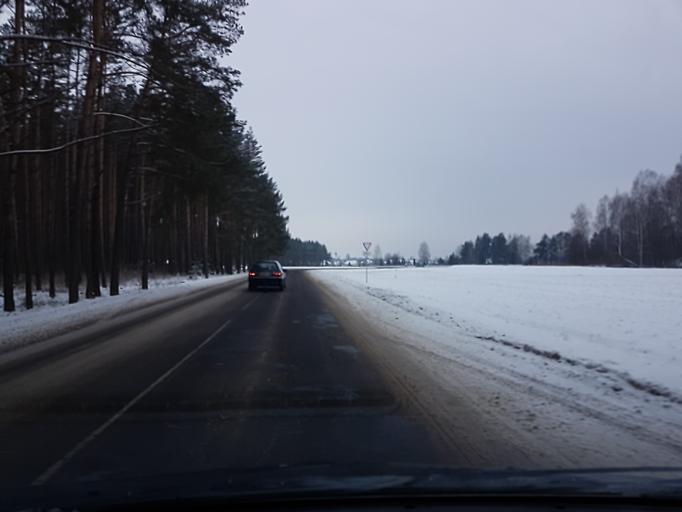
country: BY
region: Minsk
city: Rakaw
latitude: 53.9676
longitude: 27.0783
